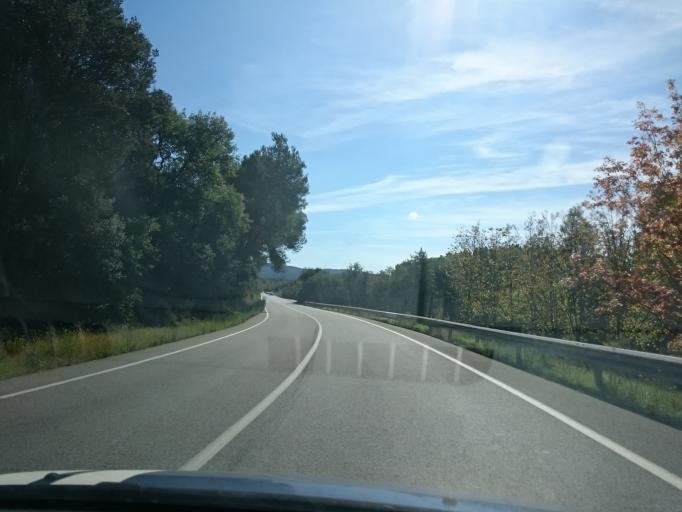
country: ES
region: Catalonia
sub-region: Provincia de Barcelona
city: Cardedeu
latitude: 41.6346
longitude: 2.3444
